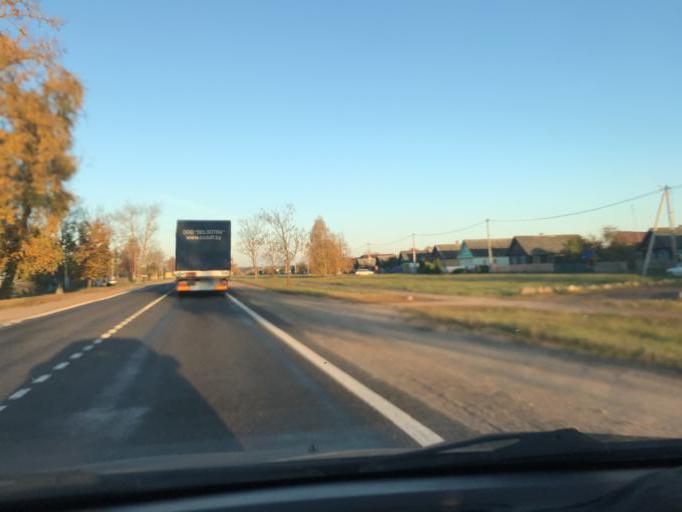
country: BY
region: Minsk
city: Staryya Darohi
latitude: 53.0395
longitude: 28.3120
